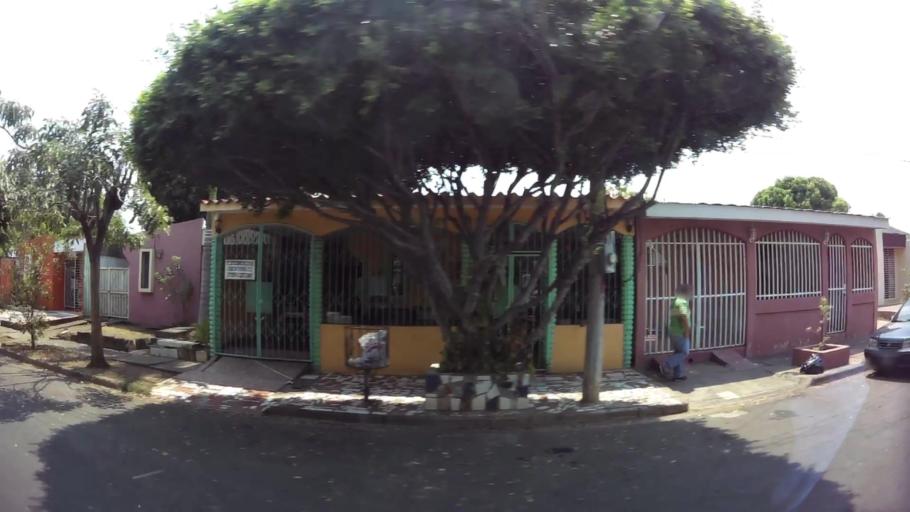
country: NI
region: Managua
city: Ciudad Sandino
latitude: 12.1523
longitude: -86.3145
